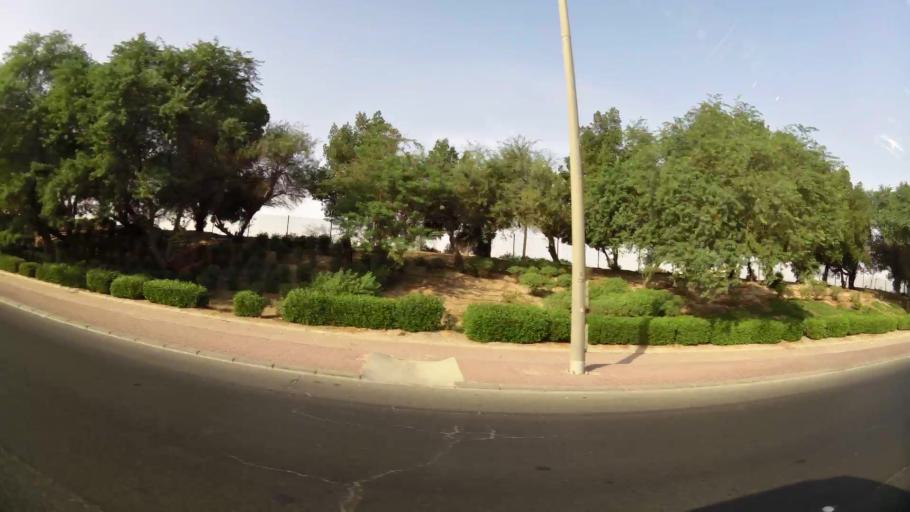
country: KW
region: Al Farwaniyah
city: Janub as Surrah
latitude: 29.2583
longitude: 47.9886
